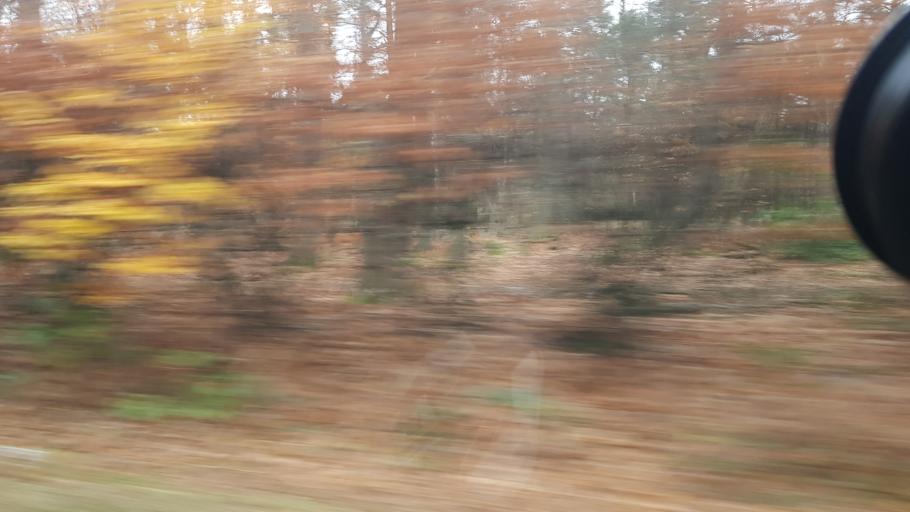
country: GB
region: England
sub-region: Hampshire
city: Fleet
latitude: 51.3065
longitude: -0.8020
